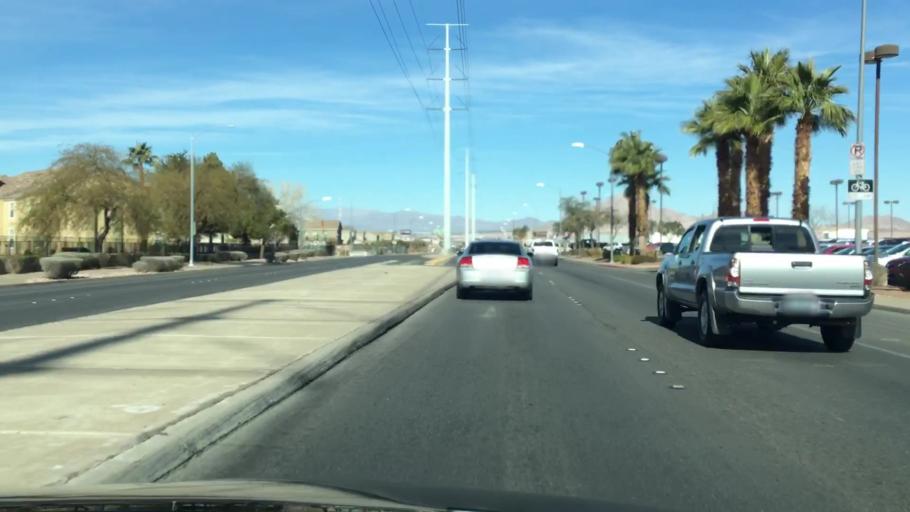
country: US
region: Nevada
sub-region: Clark County
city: Henderson
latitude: 36.0514
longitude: -115.0289
